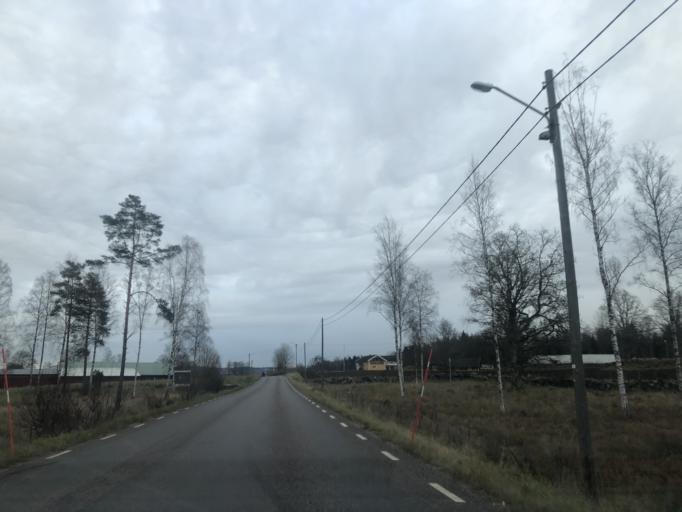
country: SE
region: Vaestra Goetaland
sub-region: Ulricehamns Kommun
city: Ulricehamn
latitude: 57.7982
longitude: 13.3551
